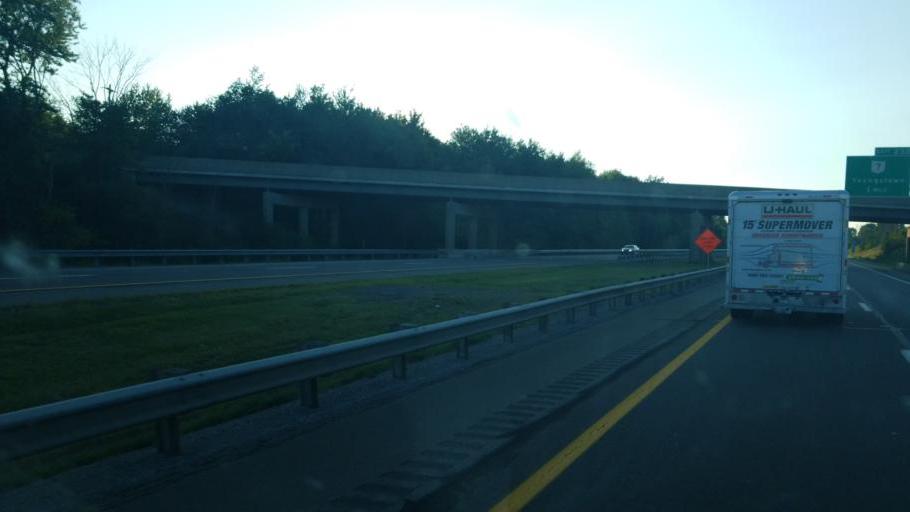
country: US
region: Ohio
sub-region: Mahoning County
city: Boardman
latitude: 40.9552
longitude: -80.6389
